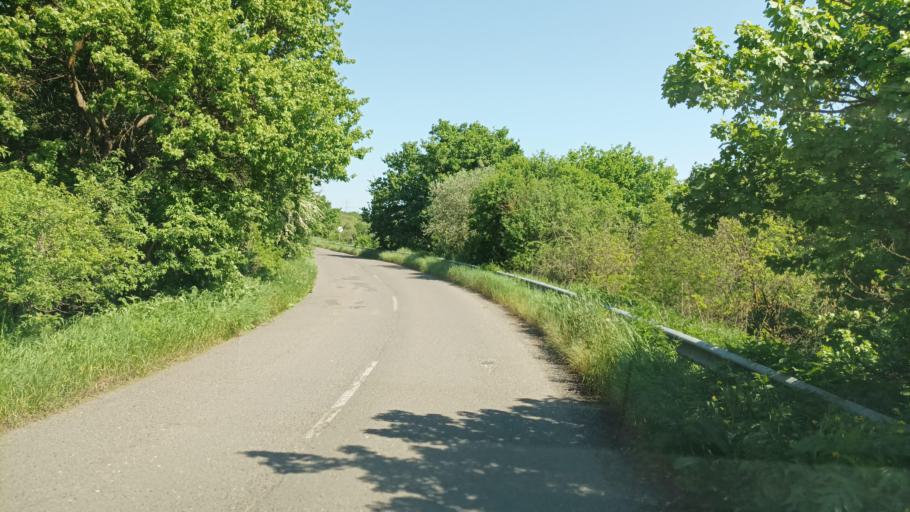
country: HU
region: Pest
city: Uri
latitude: 47.4002
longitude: 19.4918
